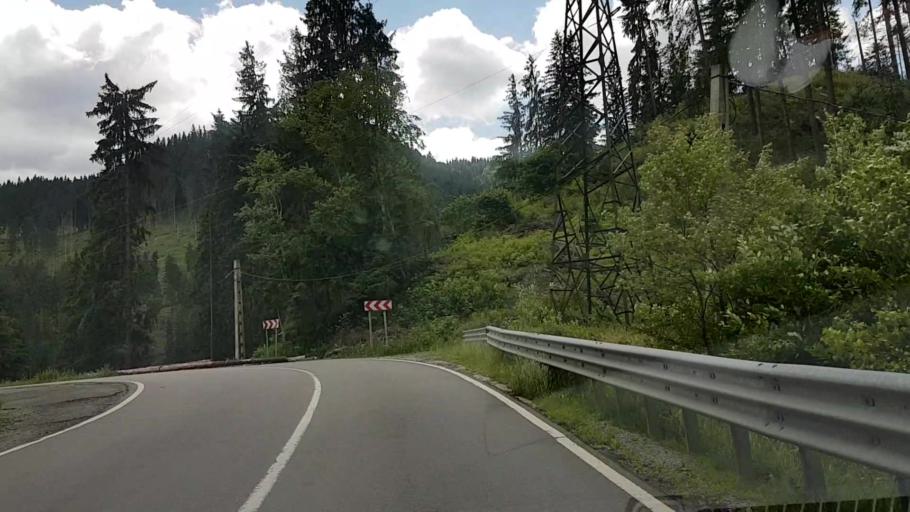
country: RO
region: Suceava
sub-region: Comuna Crucea
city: Crucea
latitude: 47.3625
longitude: 25.5919
